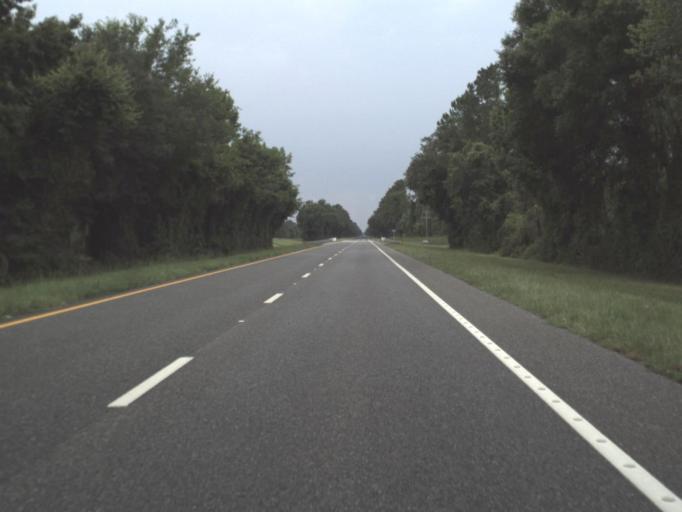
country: US
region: Florida
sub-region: Levy County
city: Bronson
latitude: 29.2938
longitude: -82.7483
